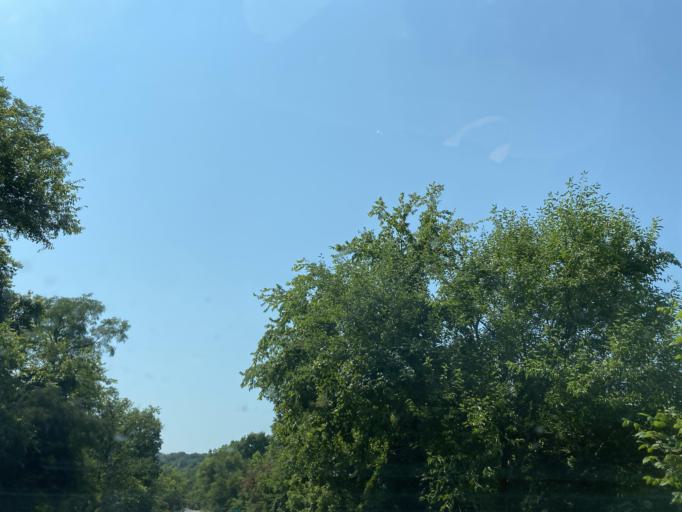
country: US
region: Kentucky
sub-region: Campbell County
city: Claryville
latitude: 38.8248
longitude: -84.4552
